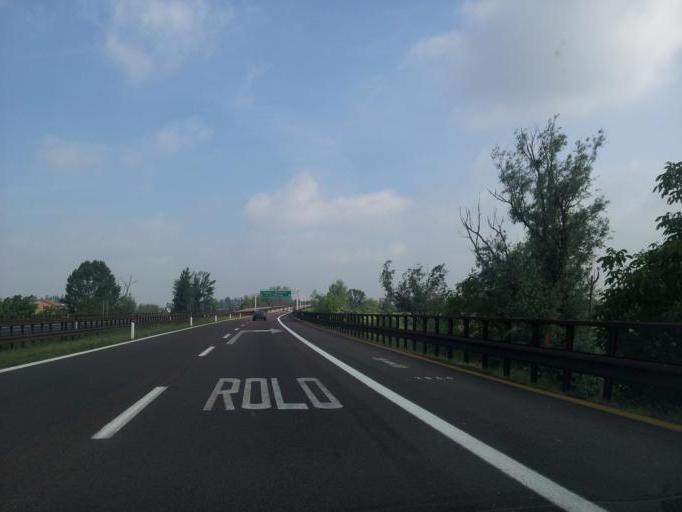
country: IT
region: Emilia-Romagna
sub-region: Provincia di Reggio Emilia
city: Rolo
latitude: 44.9043
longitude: 10.8484
